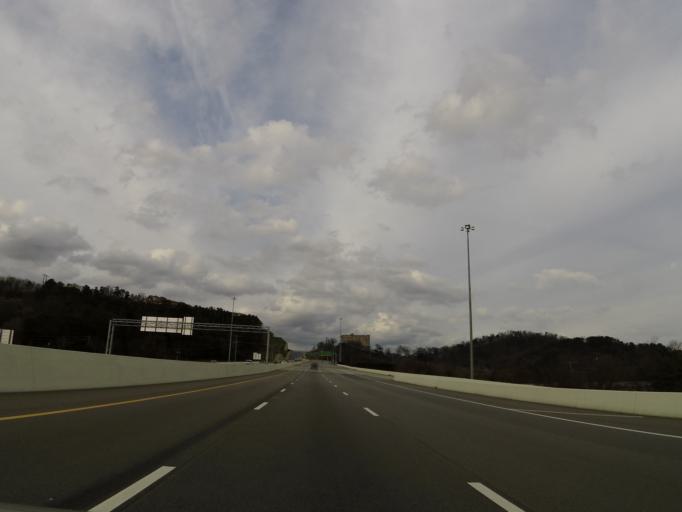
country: US
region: Tennessee
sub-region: Hamilton County
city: Chattanooga
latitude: 35.0634
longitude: -85.3178
